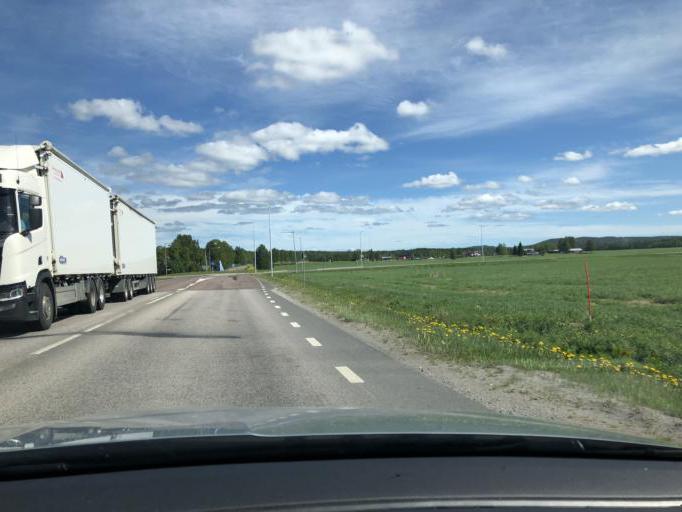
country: SE
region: Norrbotten
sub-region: Alvsbyns Kommun
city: AElvsbyn
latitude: 65.6682
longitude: 21.0442
